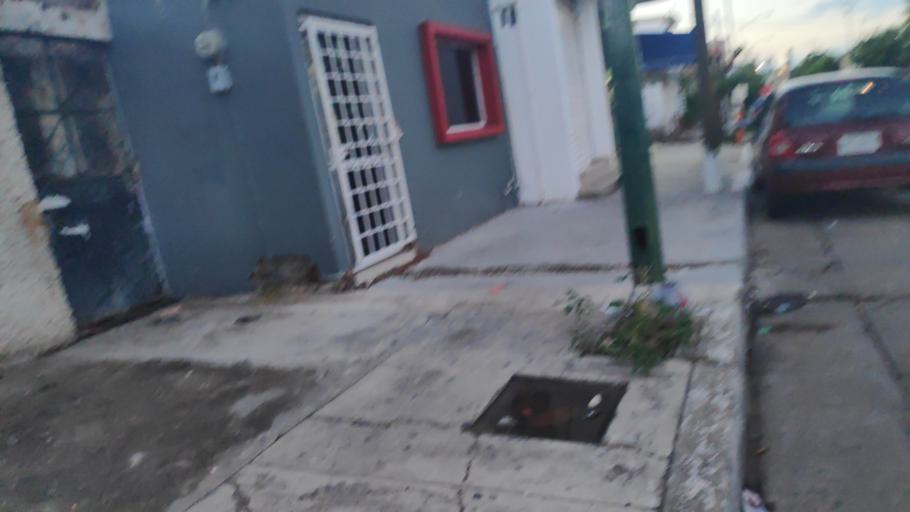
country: MX
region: Sinaloa
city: Culiacan
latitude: 24.7905
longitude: -107.4087
